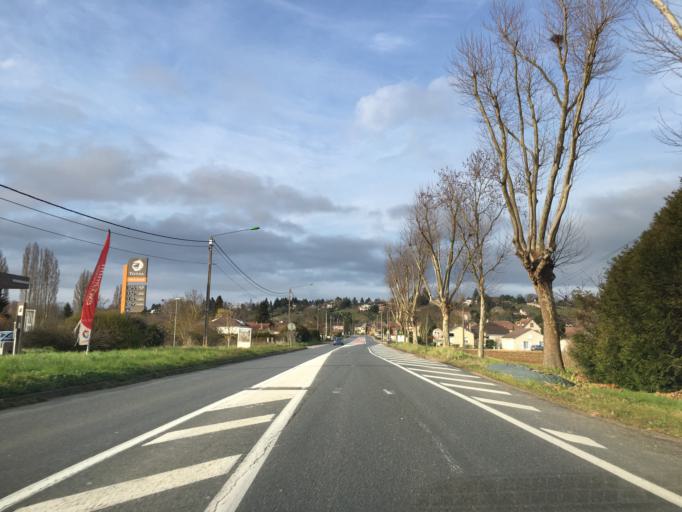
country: FR
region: Bourgogne
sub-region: Departement de l'Yonne
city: Veron
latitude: 48.1471
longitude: 3.3073
